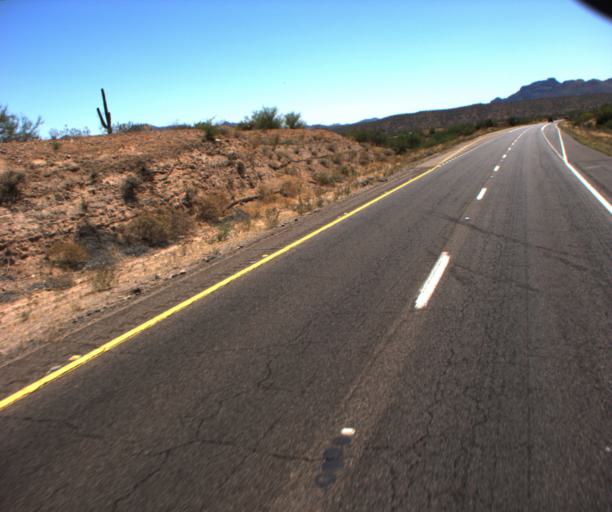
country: US
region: Arizona
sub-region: Maricopa County
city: Fountain Hills
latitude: 33.5891
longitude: -111.6011
